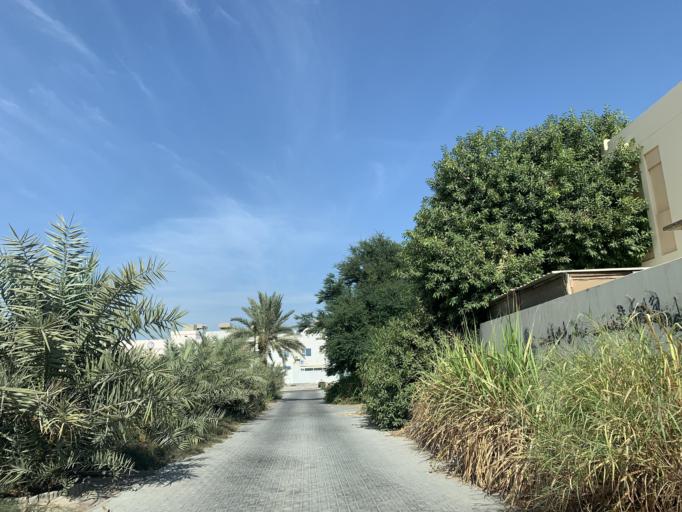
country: BH
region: Central Governorate
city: Madinat Hamad
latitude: 26.1249
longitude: 50.4749
